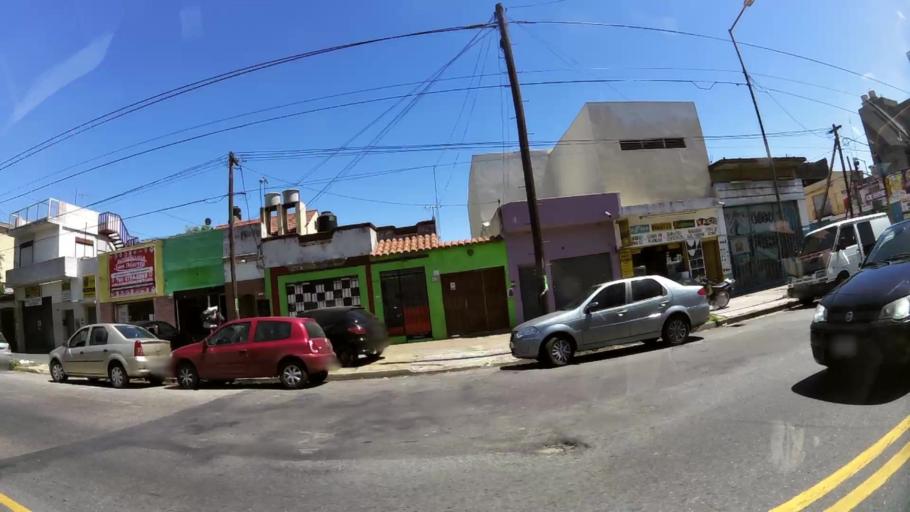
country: AR
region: Buenos Aires
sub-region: Partido de General San Martin
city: General San Martin
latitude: -34.5742
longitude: -58.5456
